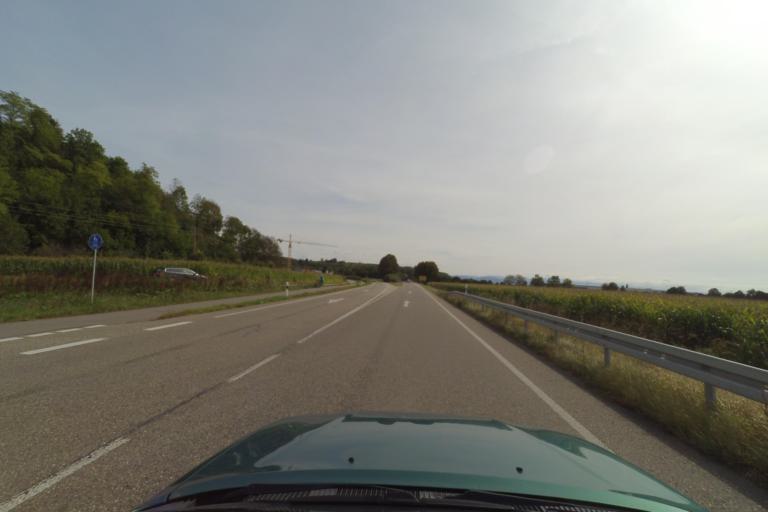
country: DE
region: Baden-Wuerttemberg
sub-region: Freiburg Region
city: Malterdingen
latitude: 48.1605
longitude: 7.7764
